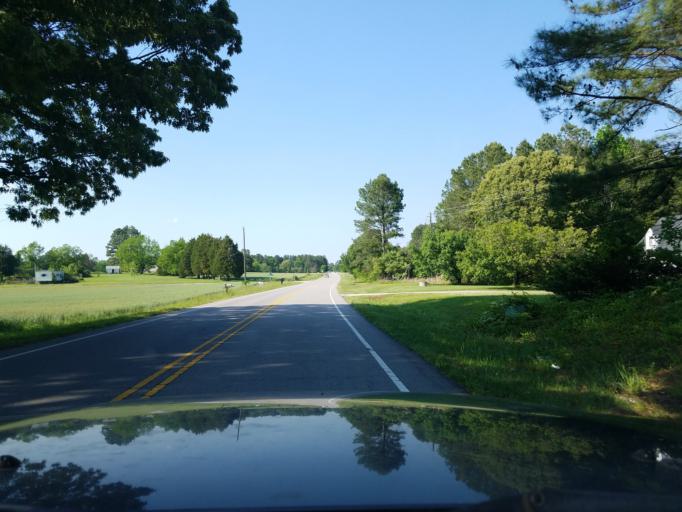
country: US
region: North Carolina
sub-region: Vance County
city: Henderson
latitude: 36.3699
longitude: -78.3723
